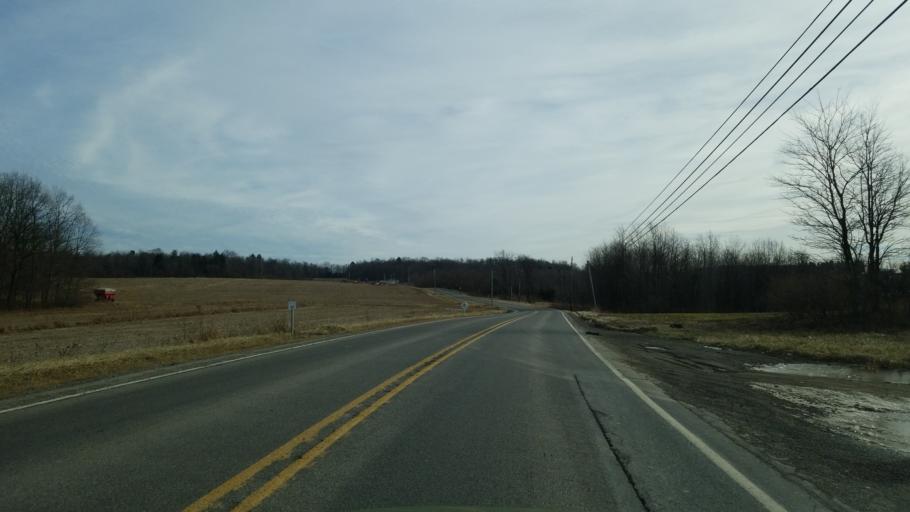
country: US
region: Pennsylvania
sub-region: Indiana County
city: Johnsonburg
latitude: 40.9208
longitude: -78.8572
